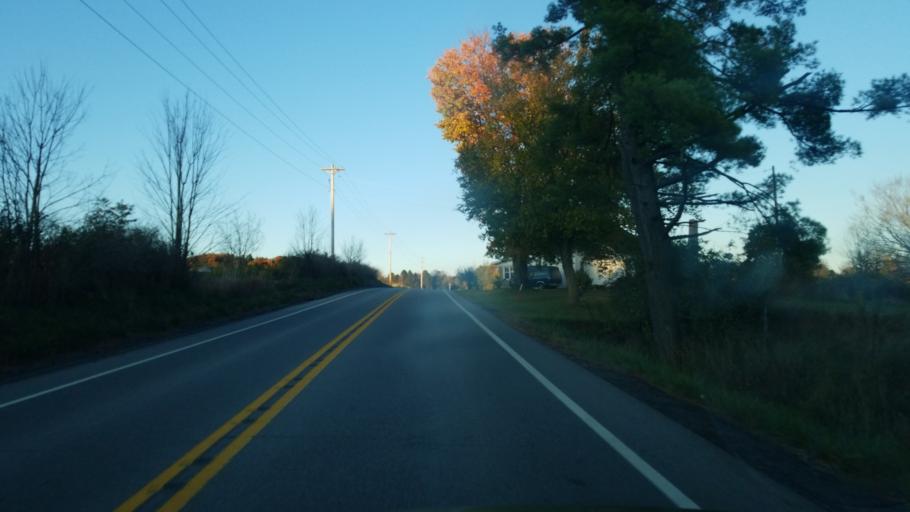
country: US
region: Pennsylvania
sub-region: Jefferson County
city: Reynoldsville
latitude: 41.0508
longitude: -78.9363
